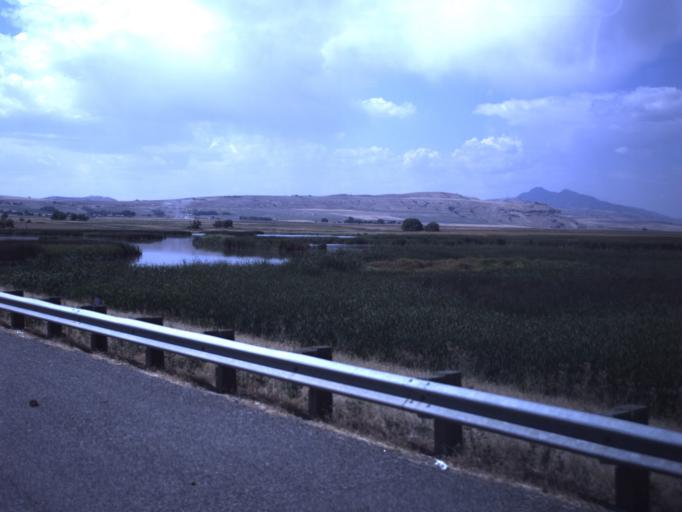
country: US
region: Utah
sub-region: Cache County
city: Mendon
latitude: 41.7462
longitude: -111.9515
